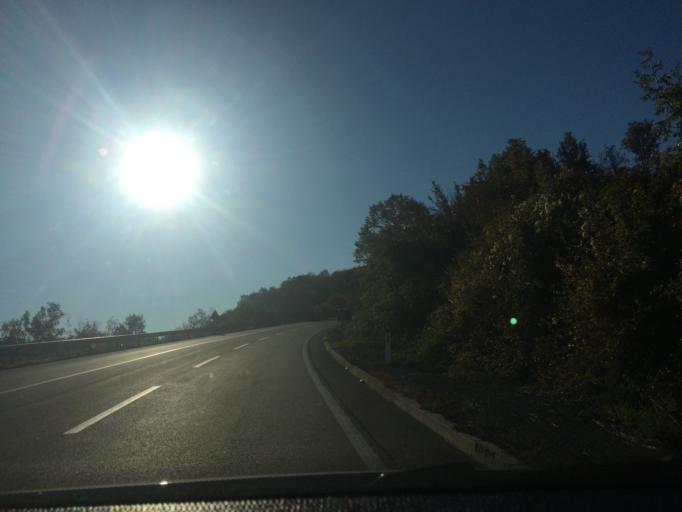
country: ME
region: Cetinje
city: Cetinje
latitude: 42.3812
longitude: 19.0582
